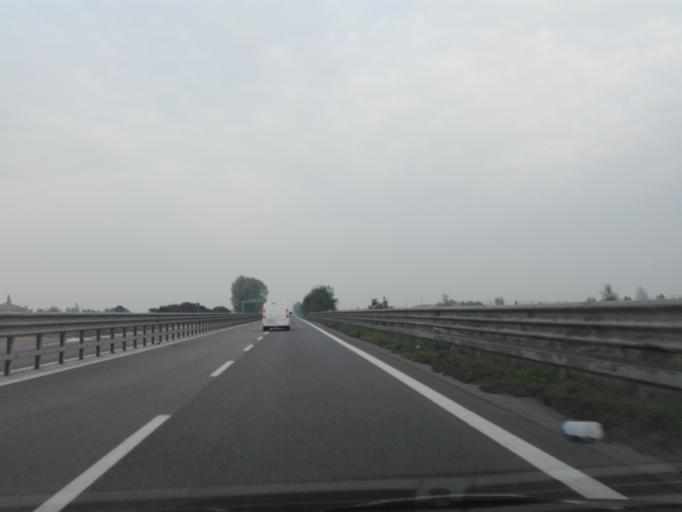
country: IT
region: Veneto
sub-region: Provincia di Rovigo
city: San Bellino
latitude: 45.0306
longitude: 11.5683
